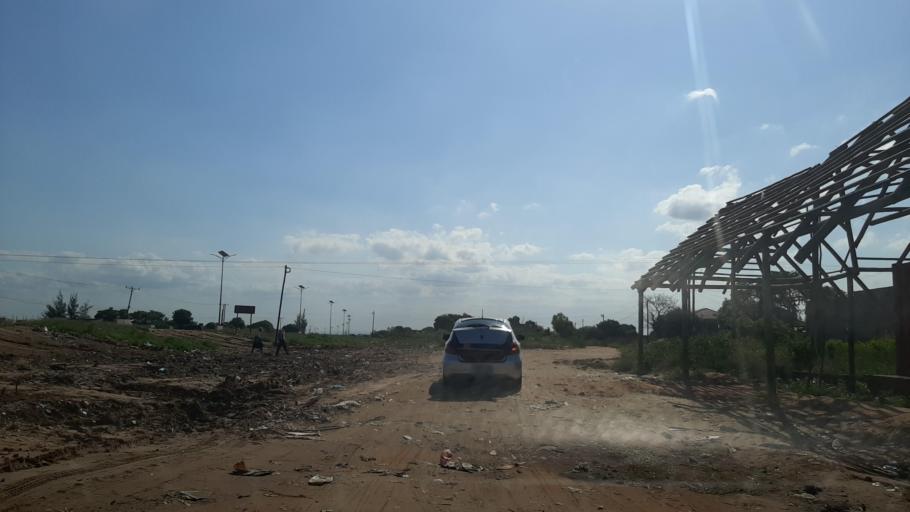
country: MZ
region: Maputo
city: Matola
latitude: -25.8152
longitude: 32.4922
